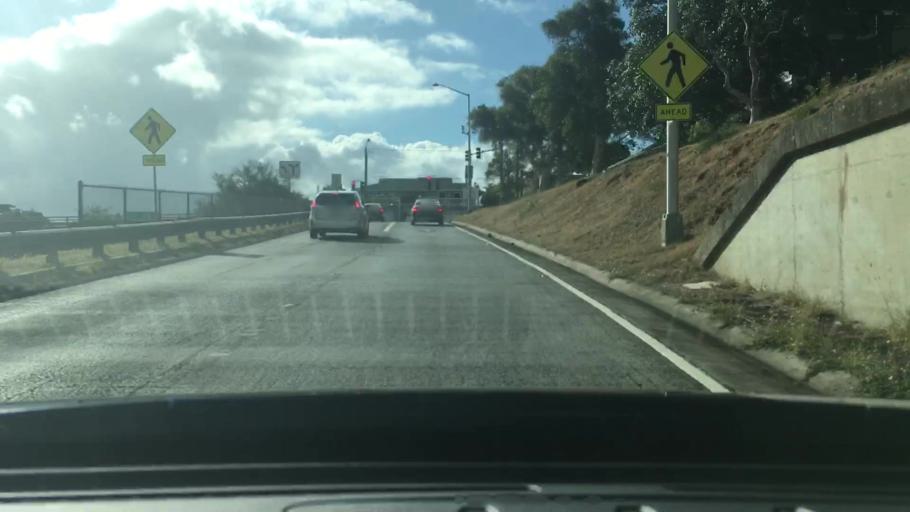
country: US
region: Hawaii
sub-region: Honolulu County
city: Honolulu
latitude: 21.2797
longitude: -157.7999
